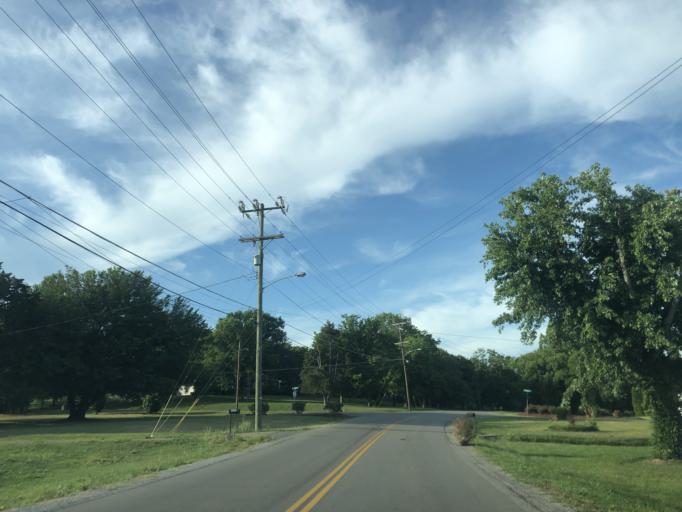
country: US
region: Tennessee
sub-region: Davidson County
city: Nashville
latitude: 36.2082
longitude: -86.8577
